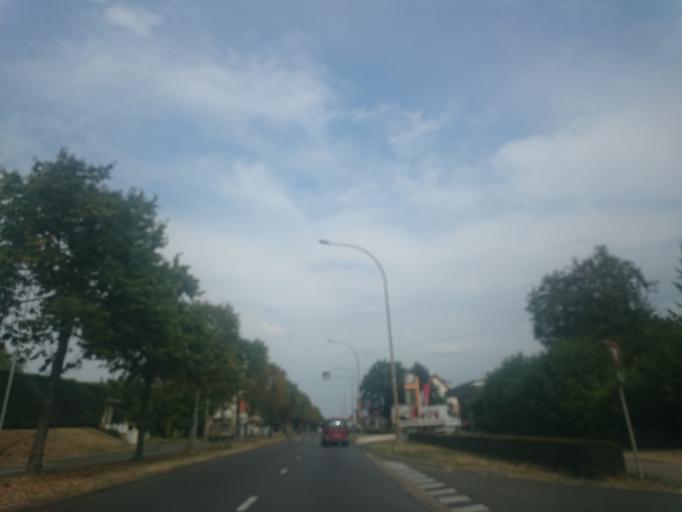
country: FR
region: Ile-de-France
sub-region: Departement de l'Essonne
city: Ris-Orangis
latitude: 48.6491
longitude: 2.4171
